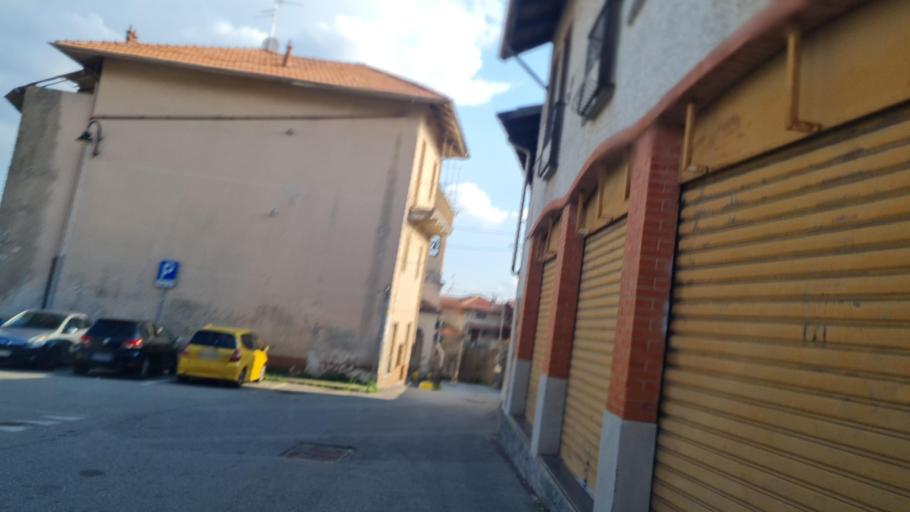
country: IT
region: Piedmont
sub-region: Provincia di Biella
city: Cossato
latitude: 45.5818
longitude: 8.1832
